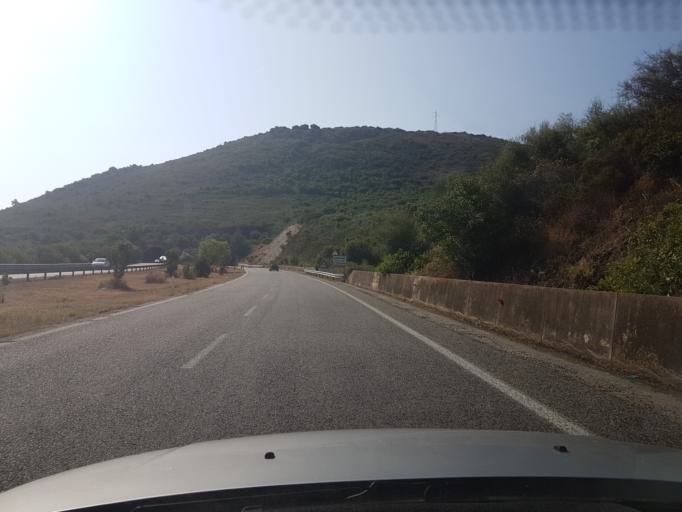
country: IT
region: Sardinia
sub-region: Provincia di Olbia-Tempio
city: San Teodoro
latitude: 40.7281
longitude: 9.6522
